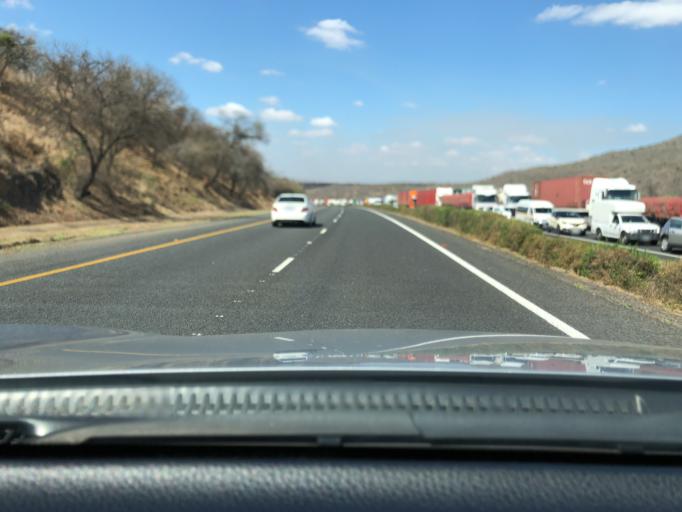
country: ZA
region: KwaZulu-Natal
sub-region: uThukela District Municipality
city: Ladysmith
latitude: -28.7316
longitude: 29.6458
